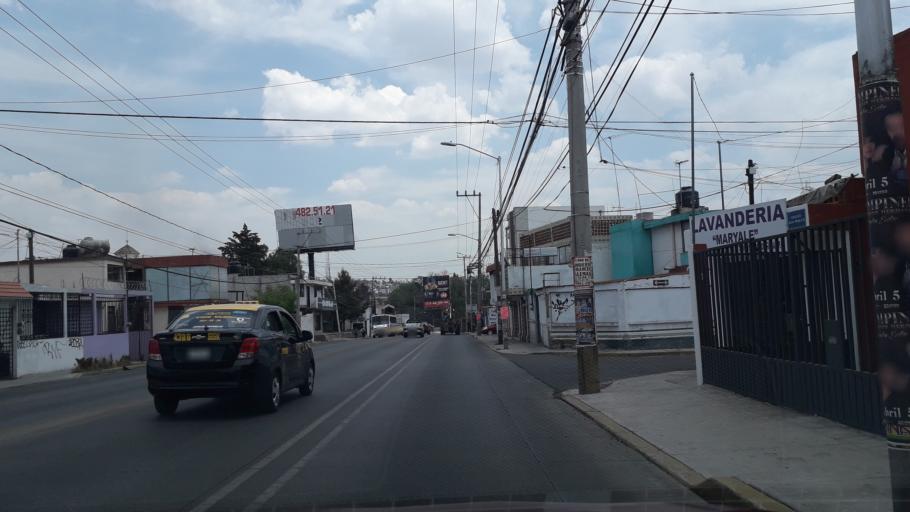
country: MX
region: Puebla
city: Puebla
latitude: 19.0131
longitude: -98.1920
